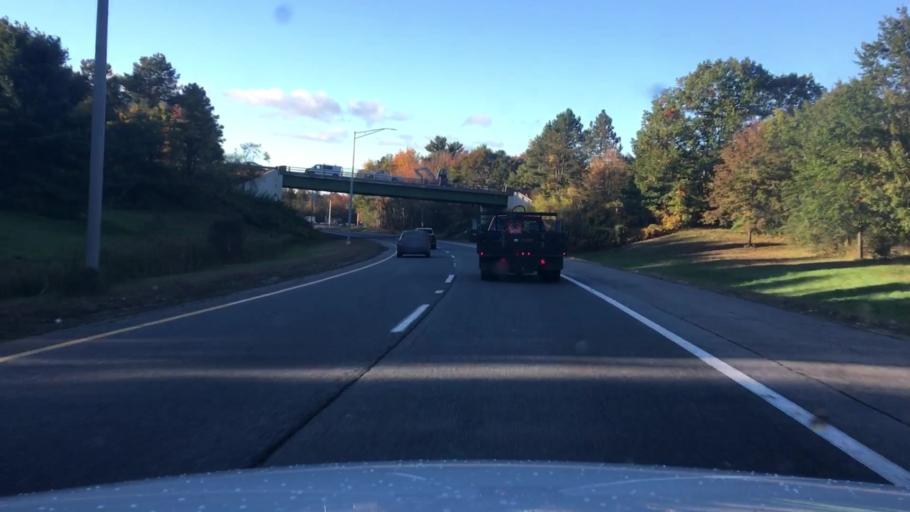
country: US
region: Maine
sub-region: Cumberland County
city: South Portland Gardens
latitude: 43.6233
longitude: -70.3559
